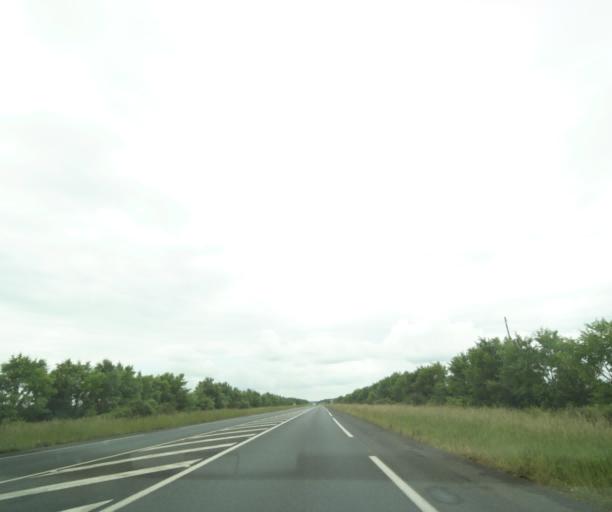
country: FR
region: Poitou-Charentes
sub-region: Departement des Deux-Sevres
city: Saint-Varent
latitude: 46.8773
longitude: -0.1962
